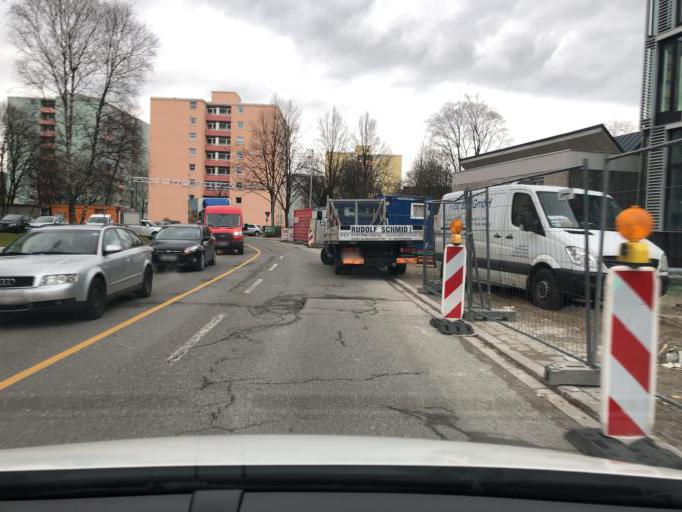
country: DE
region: Bavaria
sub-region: Upper Bavaria
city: Rosenheim
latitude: 47.8551
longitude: 12.1134
